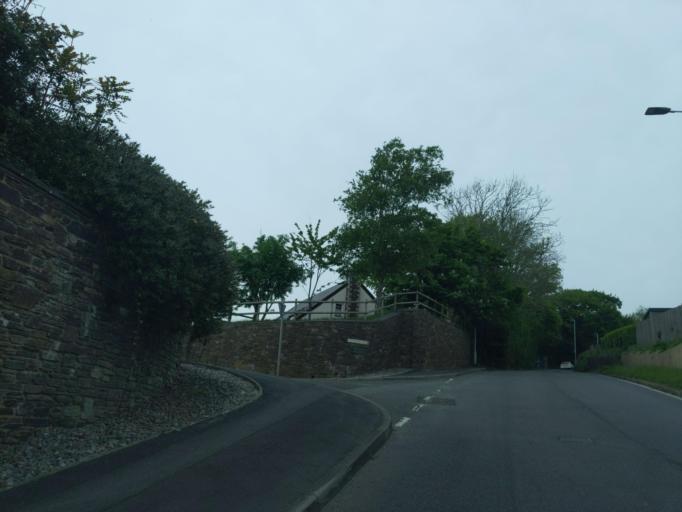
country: GB
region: England
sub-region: Devon
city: Plympton
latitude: 50.3983
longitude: -4.0541
